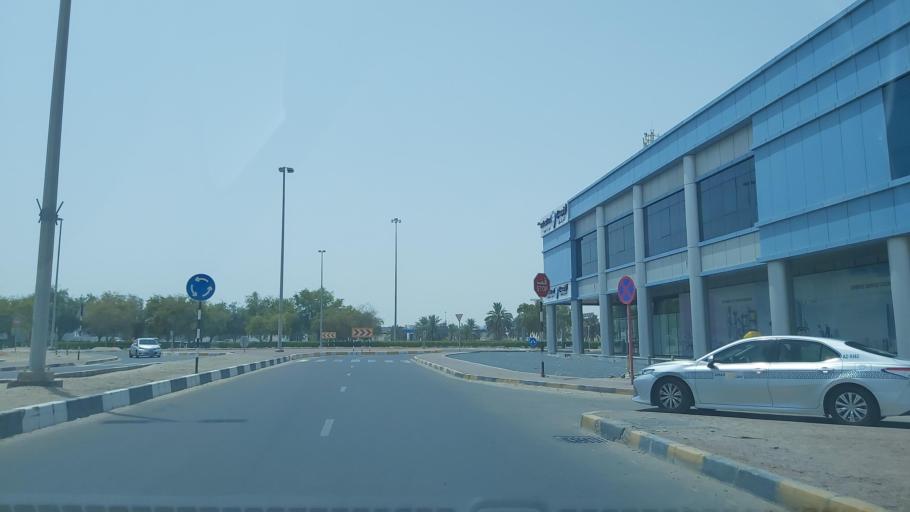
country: AE
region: Abu Dhabi
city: Abu Dhabi
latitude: 24.3751
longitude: 54.5203
